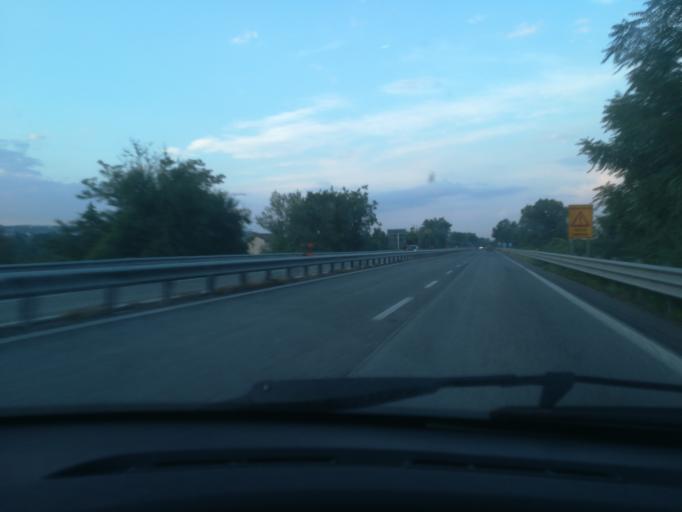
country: IT
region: The Marches
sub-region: Provincia di Macerata
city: Sforzacosta
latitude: 43.2523
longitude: 13.4424
